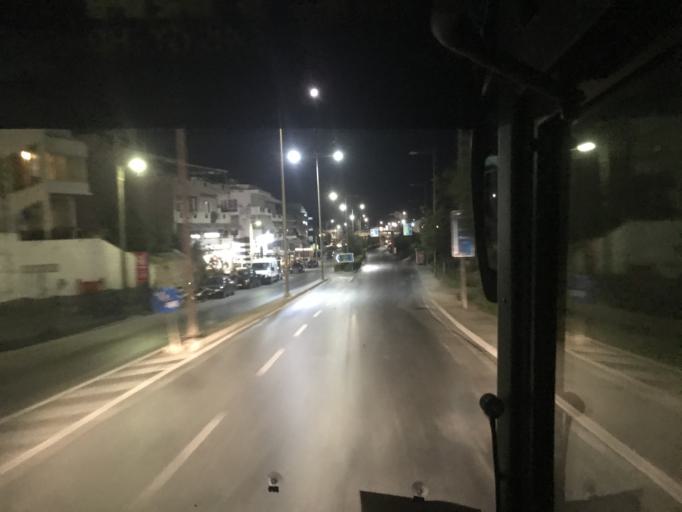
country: GR
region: Crete
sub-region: Nomos Irakleiou
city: Irakleion
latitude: 35.3240
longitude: 25.1403
